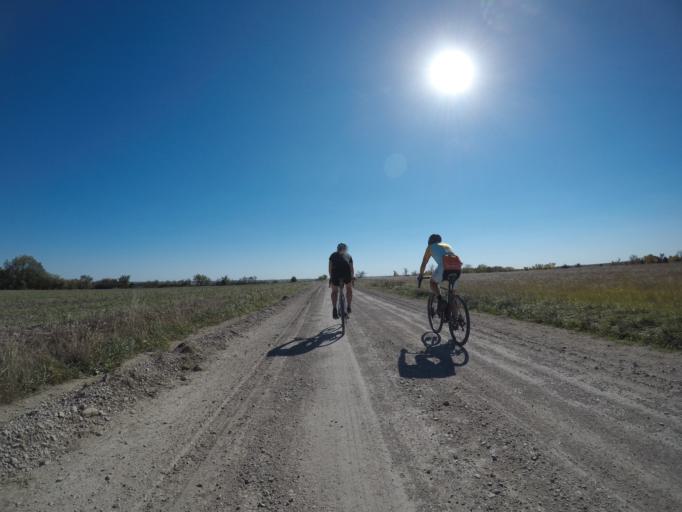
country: US
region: Kansas
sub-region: Wabaunsee County
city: Alma
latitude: 38.9689
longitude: -96.4736
